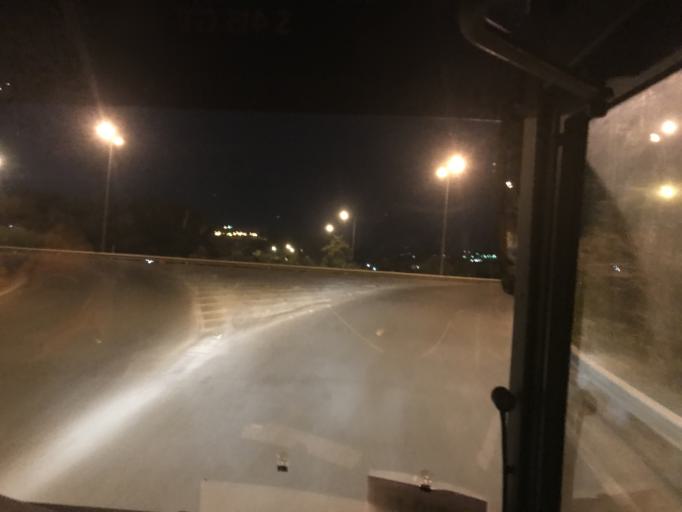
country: GR
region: Crete
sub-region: Nomos Irakleiou
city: Nea Alikarnassos
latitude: 35.3328
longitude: 25.1575
